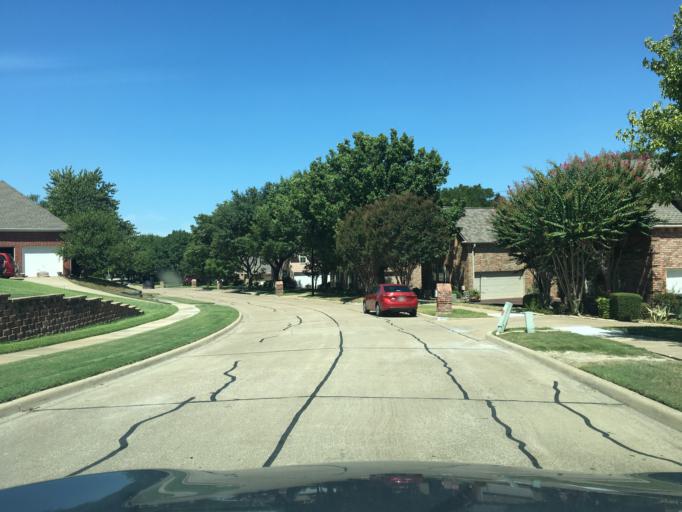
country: US
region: Texas
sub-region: Dallas County
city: Sachse
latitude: 32.9687
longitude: -96.6289
